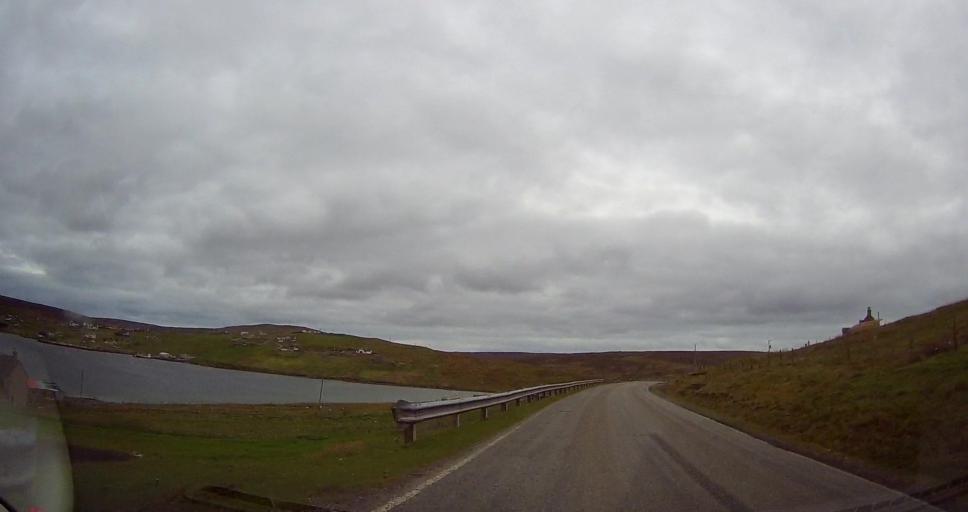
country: GB
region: Scotland
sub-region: Shetland Islands
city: Shetland
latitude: 60.6109
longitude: -1.0741
